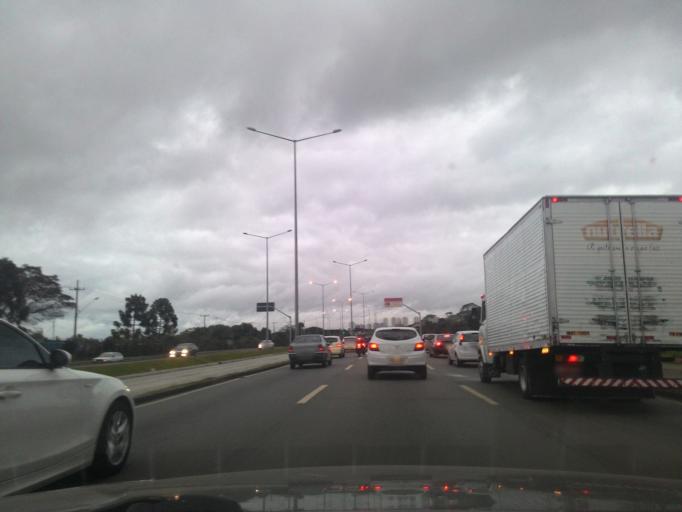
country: BR
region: Parana
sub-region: Curitiba
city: Curitiba
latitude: -25.4627
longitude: -49.2510
